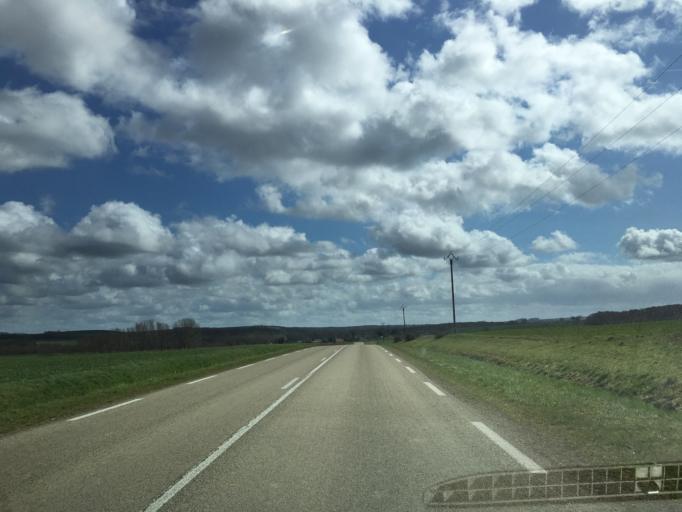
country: FR
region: Bourgogne
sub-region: Departement de l'Yonne
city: Aillant-sur-Tholon
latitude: 47.8500
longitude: 3.3809
